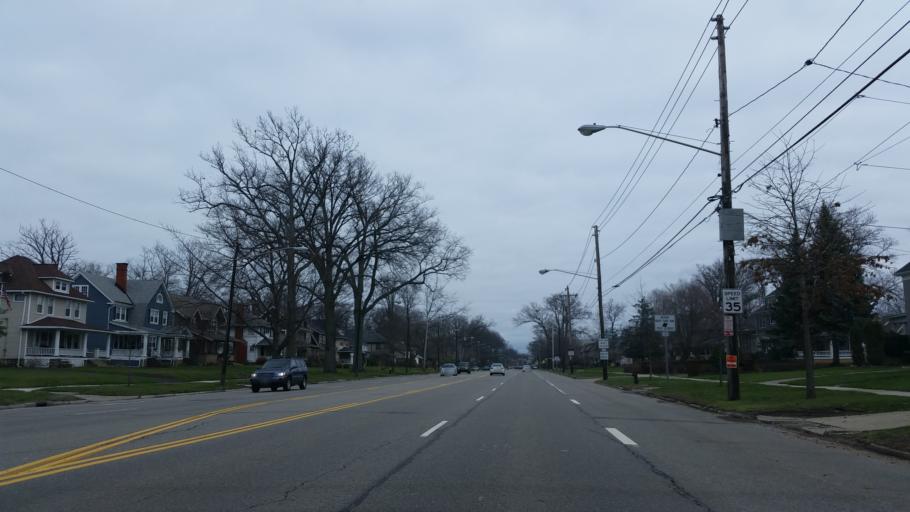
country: US
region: Ohio
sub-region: Cuyahoga County
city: Lakewood
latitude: 41.4916
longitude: -81.7952
